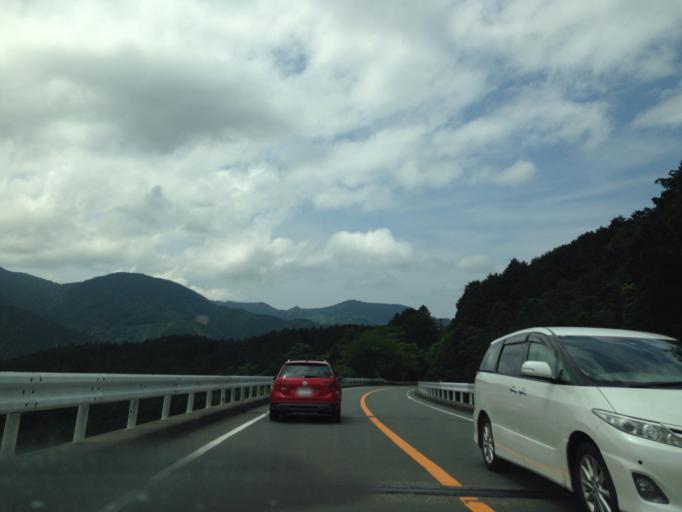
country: JP
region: Shizuoka
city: Heda
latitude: 34.9160
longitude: 138.8247
